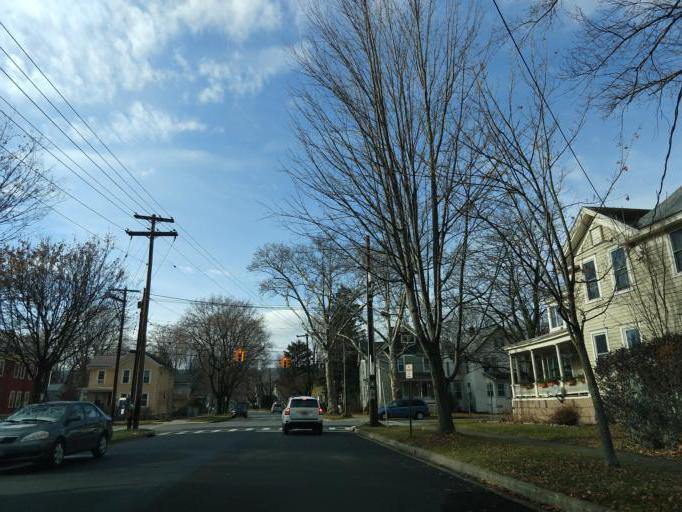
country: US
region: New York
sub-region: Tompkins County
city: Ithaca
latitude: 42.4521
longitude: -76.4993
